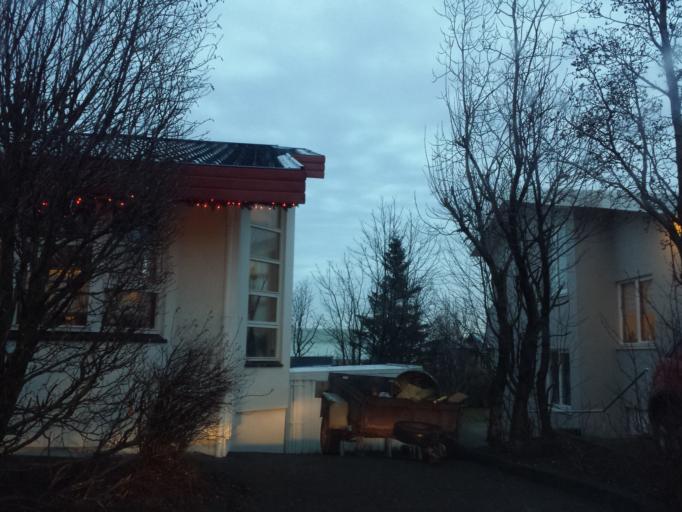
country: IS
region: Capital Region
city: Mosfellsbaer
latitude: 64.1356
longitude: -21.7752
